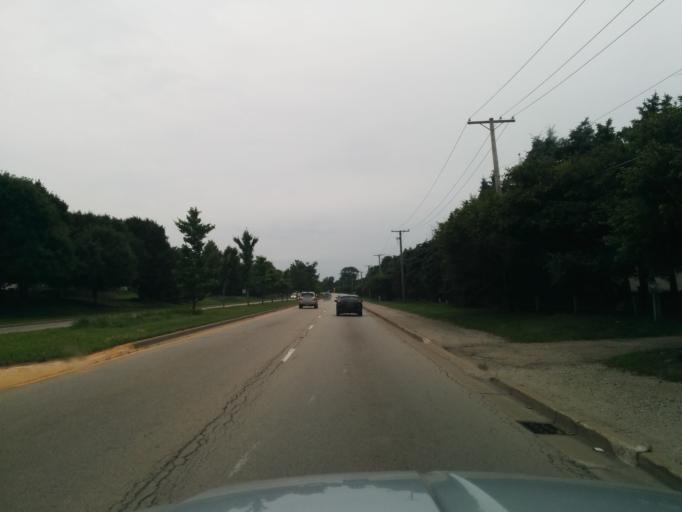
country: US
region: Illinois
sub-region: DuPage County
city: Warrenville
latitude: 41.7893
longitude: -88.2414
